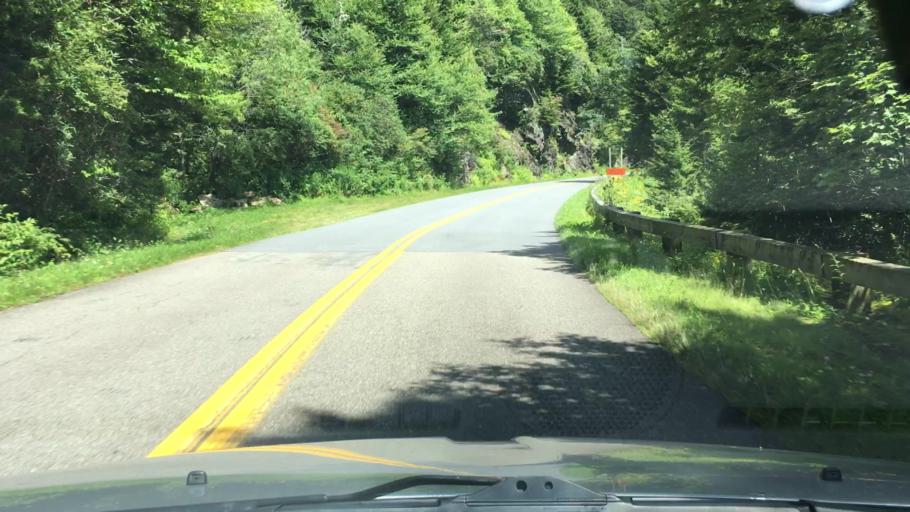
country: US
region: North Carolina
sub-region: Buncombe County
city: Black Mountain
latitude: 35.7336
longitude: -82.3176
